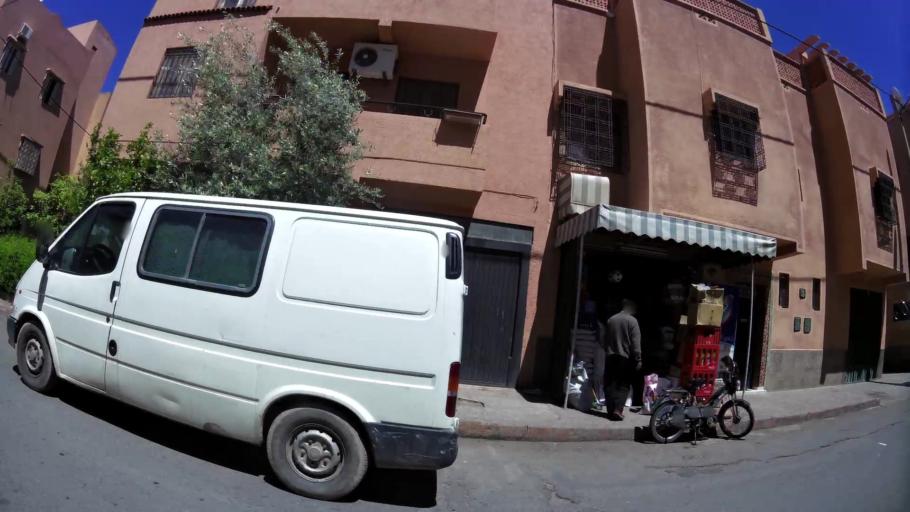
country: MA
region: Marrakech-Tensift-Al Haouz
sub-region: Marrakech
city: Marrakesh
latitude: 31.6294
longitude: -8.0531
